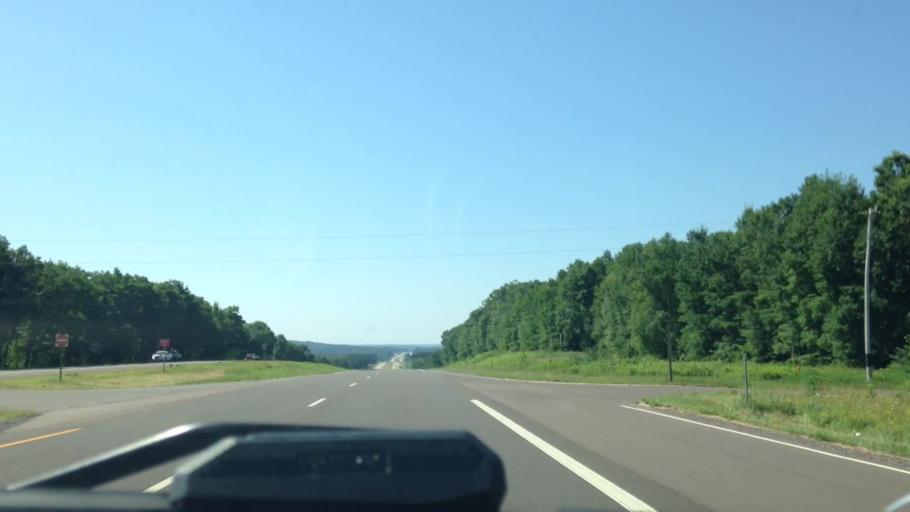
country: US
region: Wisconsin
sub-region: Washburn County
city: Spooner
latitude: 45.9357
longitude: -91.8281
